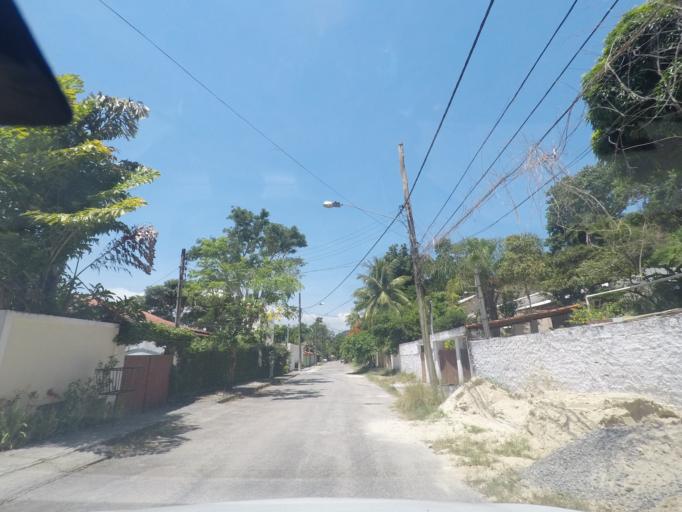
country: BR
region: Rio de Janeiro
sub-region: Niteroi
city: Niteroi
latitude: -22.9691
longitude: -43.0405
